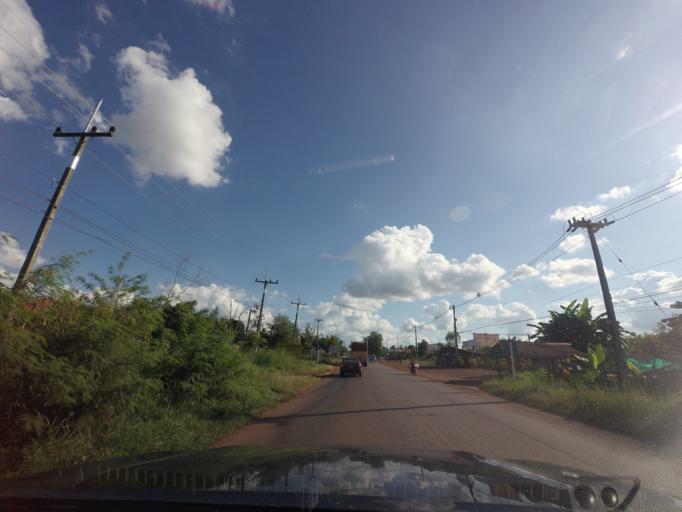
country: TH
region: Changwat Udon Thani
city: Ban Dung
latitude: 17.7354
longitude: 103.2535
